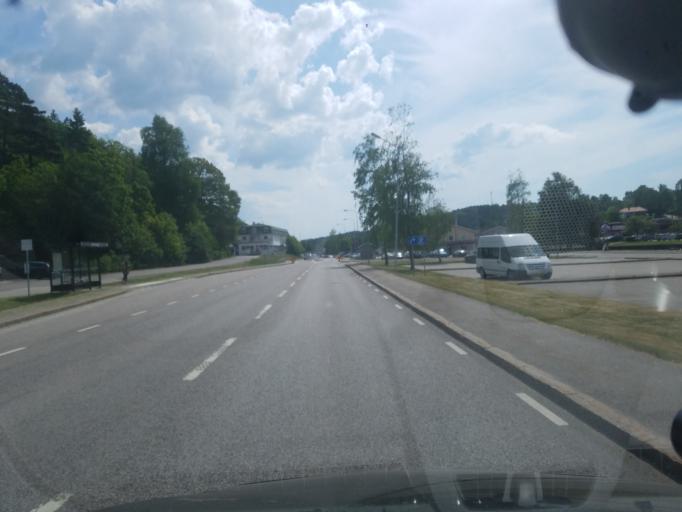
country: SE
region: Vaestra Goetaland
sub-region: Orust
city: Henan
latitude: 58.2395
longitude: 11.6801
